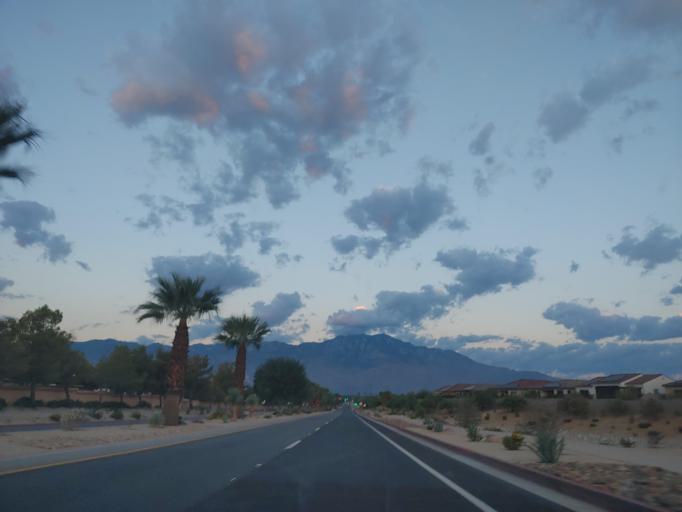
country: US
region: California
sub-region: Riverside County
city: Thousand Palms
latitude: 33.8018
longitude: -116.4132
